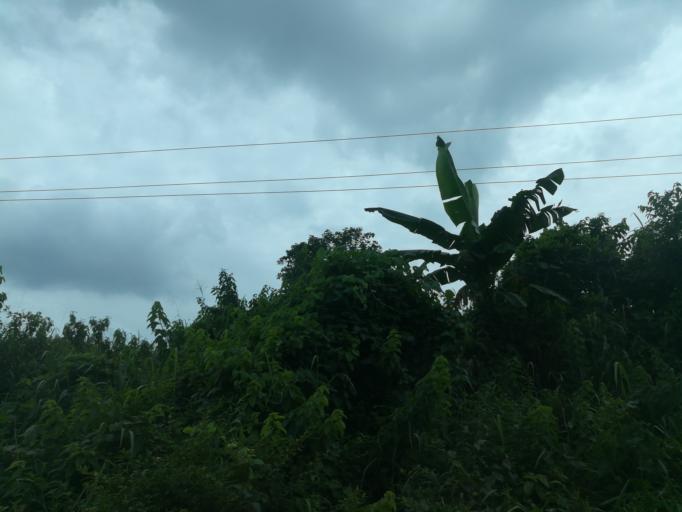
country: NG
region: Ogun
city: Odogbolu
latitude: 6.6568
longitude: 3.7120
